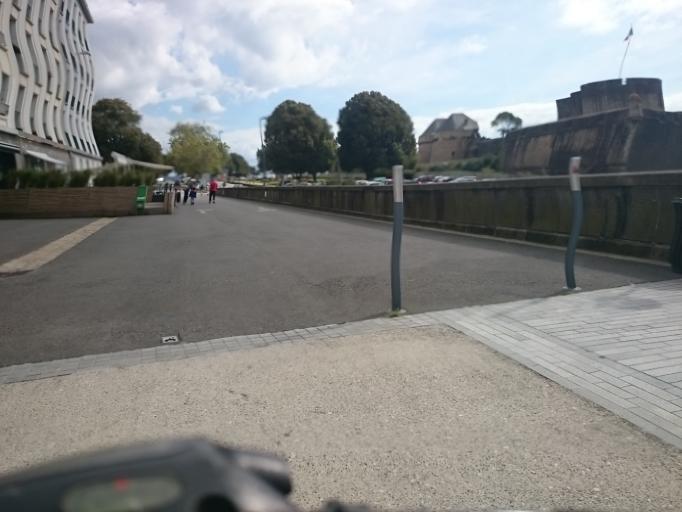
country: FR
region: Brittany
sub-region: Departement du Finistere
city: Brest
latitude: 48.3840
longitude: -4.4941
